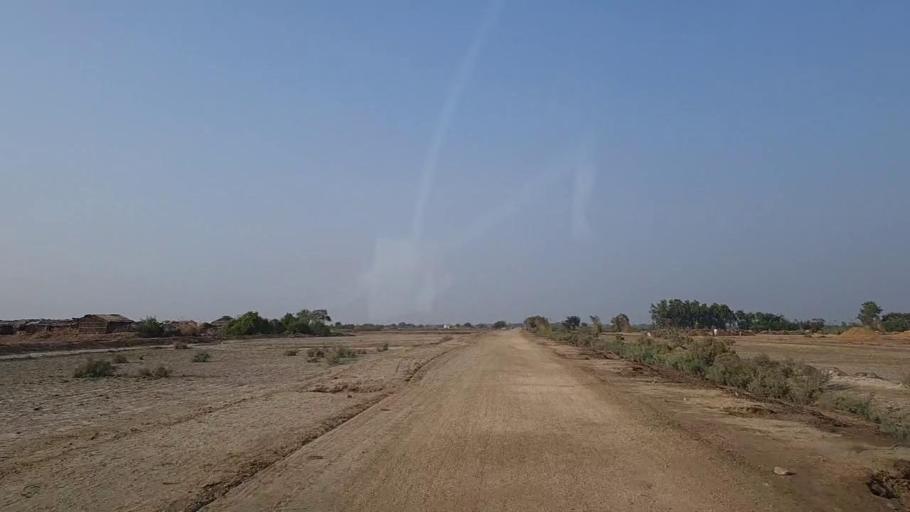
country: PK
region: Sindh
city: Mirpur Sakro
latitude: 24.6306
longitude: 67.7678
